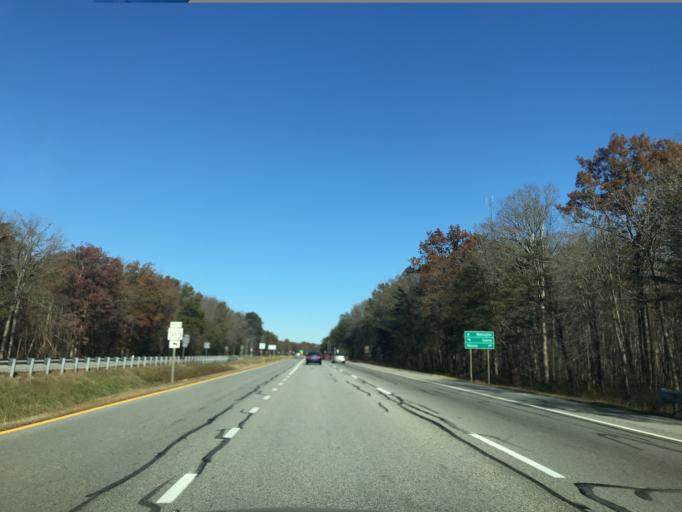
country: US
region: Delaware
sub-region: New Castle County
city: Townsend
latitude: 39.3163
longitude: -75.8474
